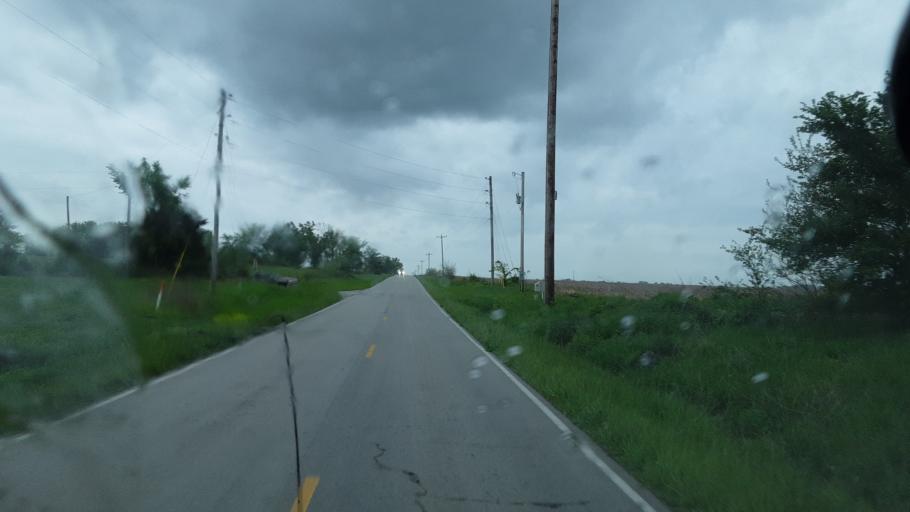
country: US
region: Missouri
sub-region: Boone County
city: Centralia
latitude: 39.4104
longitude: -92.2102
